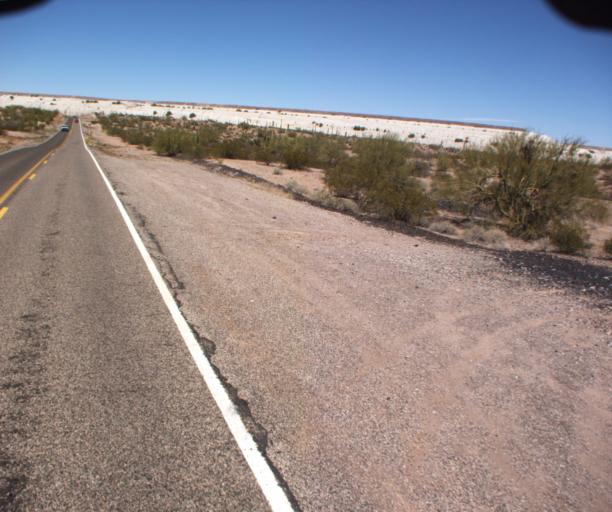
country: US
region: Arizona
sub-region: Pima County
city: Ajo
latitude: 32.3628
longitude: -112.8355
